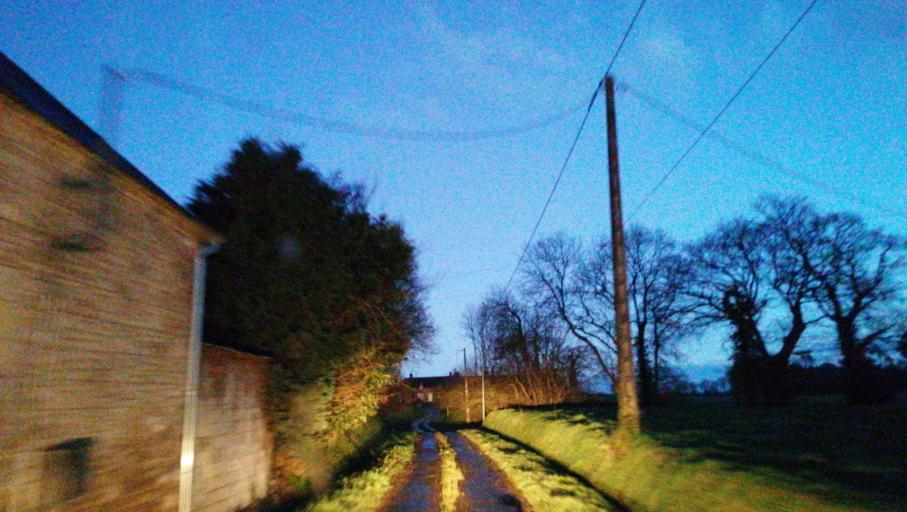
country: FR
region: Brittany
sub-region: Departement des Cotes-d'Armor
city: Plelo
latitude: 48.5628
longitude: -2.9676
